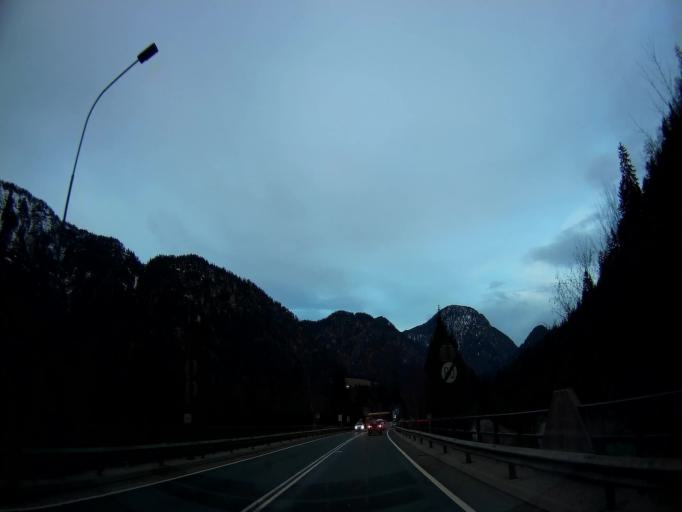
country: AT
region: Salzburg
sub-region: Politischer Bezirk Zell am See
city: Unken
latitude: 47.6530
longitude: 12.7397
